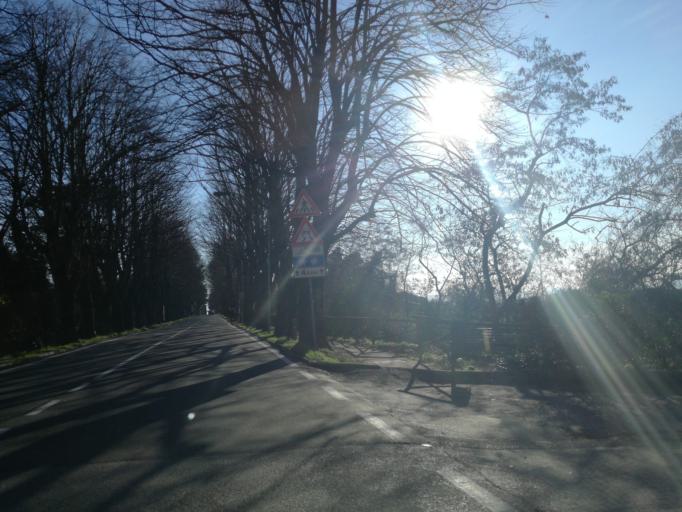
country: IT
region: Umbria
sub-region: Provincia di Perugia
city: Perugia
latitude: 43.0950
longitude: 12.3983
